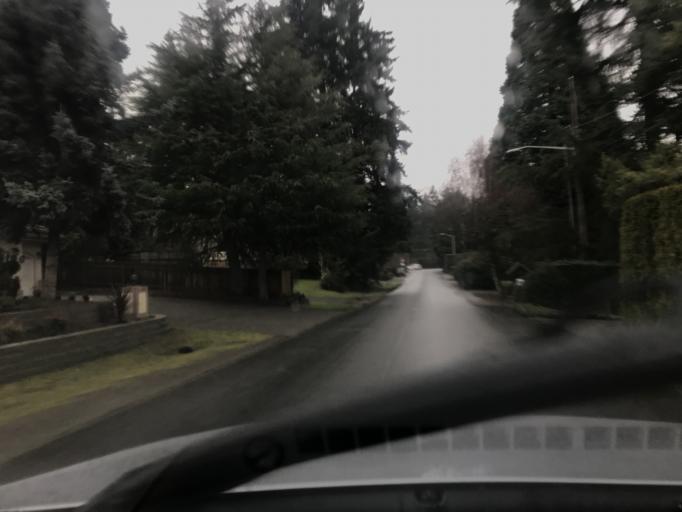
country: US
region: Washington
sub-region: King County
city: Bellevue
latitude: 47.6158
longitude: -122.1650
